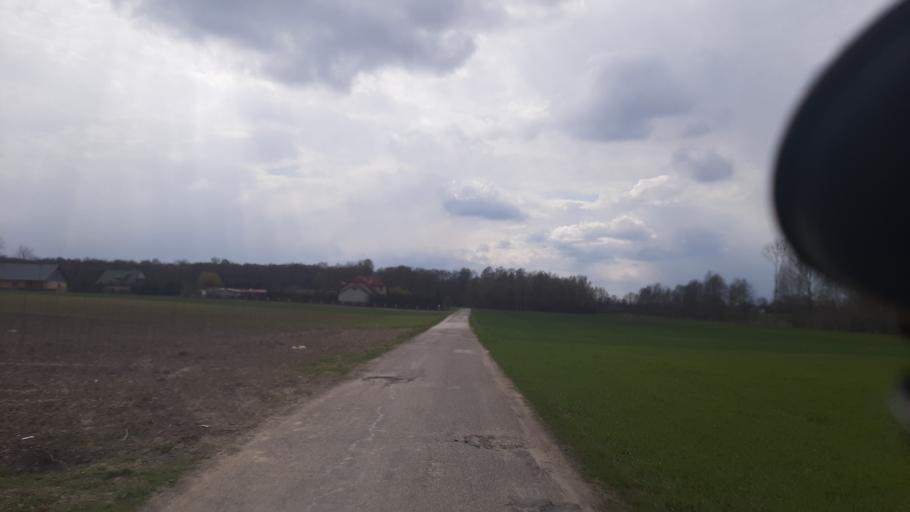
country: PL
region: Lublin Voivodeship
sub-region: Powiat lubelski
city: Jastkow
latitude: 51.3574
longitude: 22.4381
